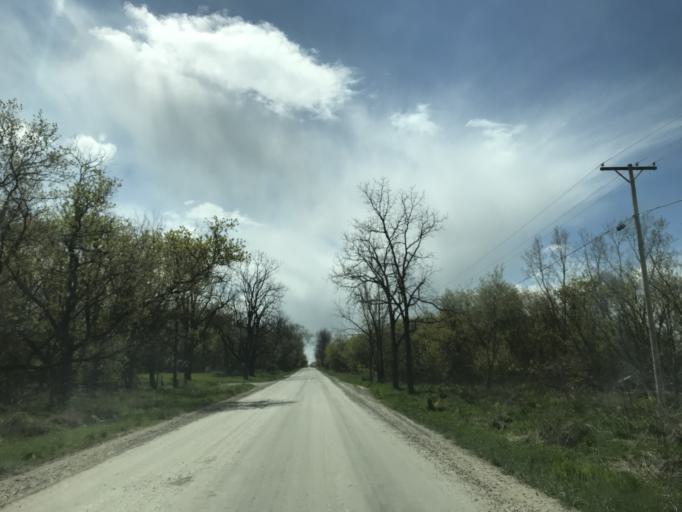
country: US
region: Michigan
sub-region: Oakland County
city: South Lyon
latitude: 42.3884
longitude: -83.6300
